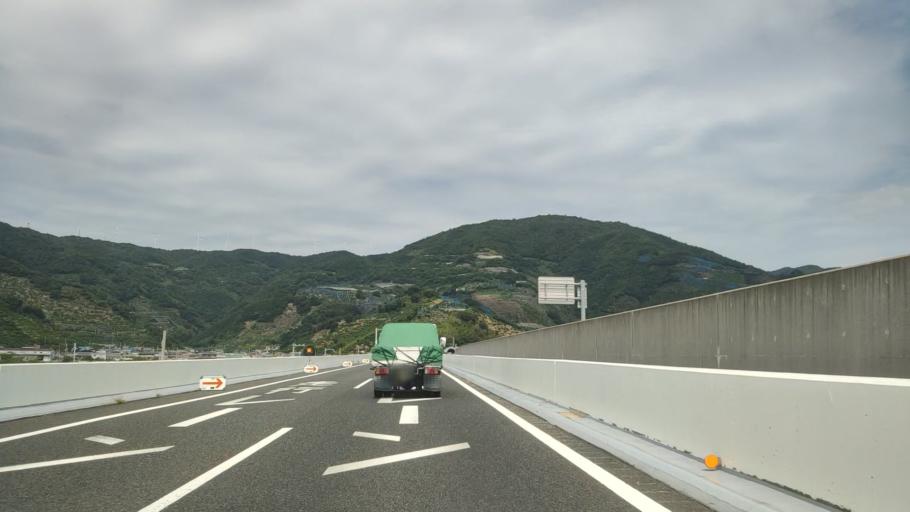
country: JP
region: Wakayama
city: Kainan
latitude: 34.0703
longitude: 135.2004
